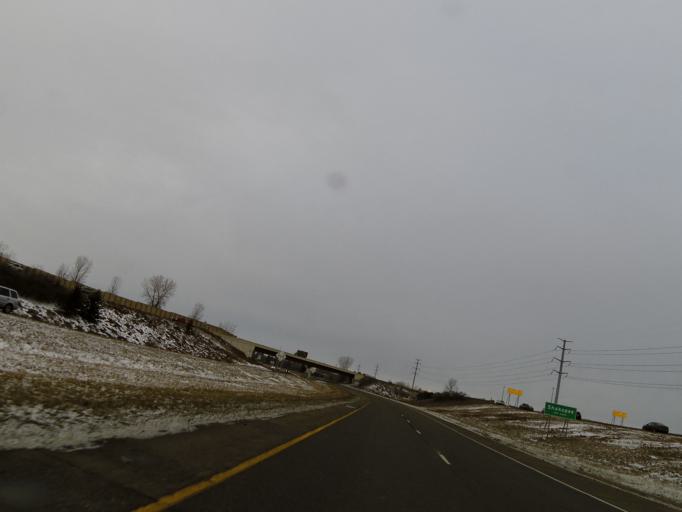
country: US
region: Minnesota
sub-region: Scott County
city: Savage
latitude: 44.7840
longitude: -93.3975
